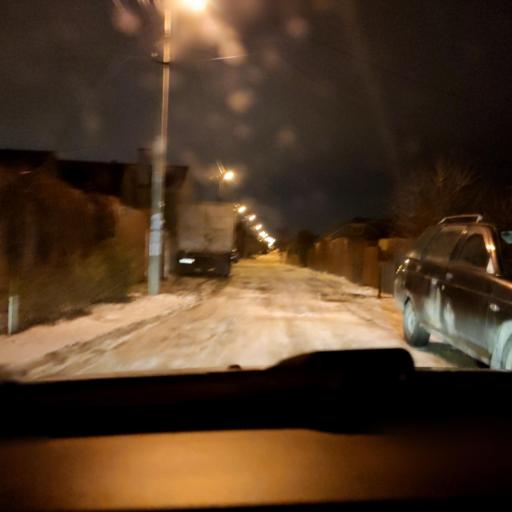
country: RU
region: Voronezj
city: Pridonskoy
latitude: 51.6846
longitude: 39.0702
